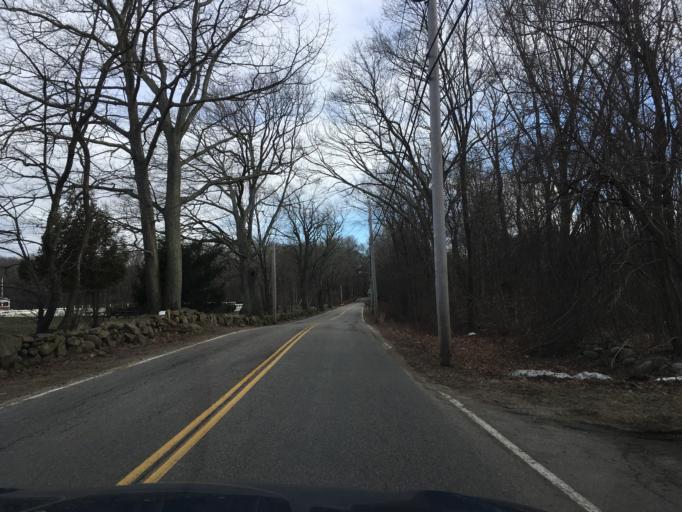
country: US
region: Rhode Island
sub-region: Washington County
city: Exeter
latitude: 41.6192
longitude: -71.5102
